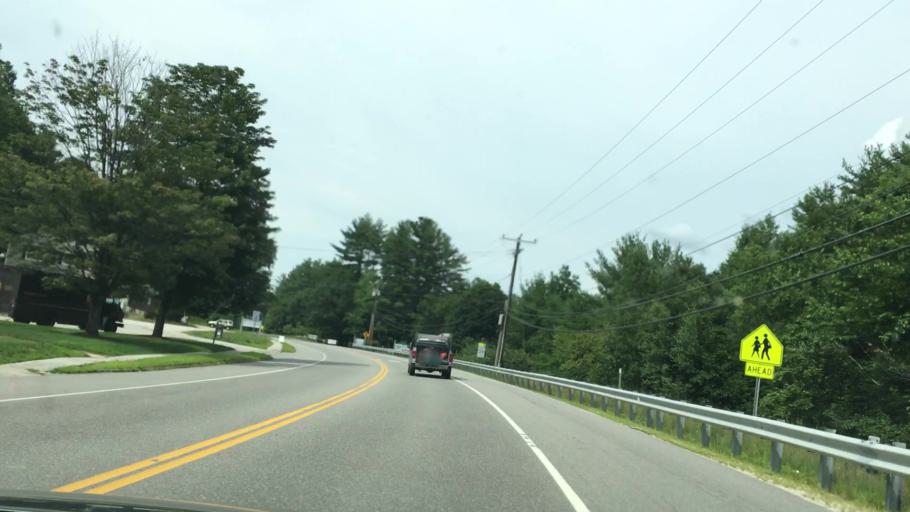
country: US
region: New Hampshire
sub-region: Hillsborough County
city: Peterborough
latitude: 42.9029
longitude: -71.9368
